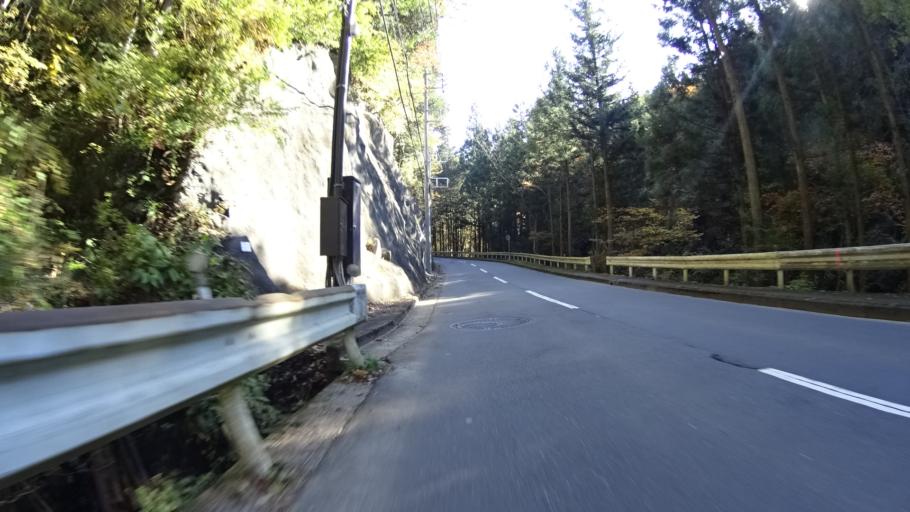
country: JP
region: Yamanashi
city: Uenohara
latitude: 35.7083
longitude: 139.0961
